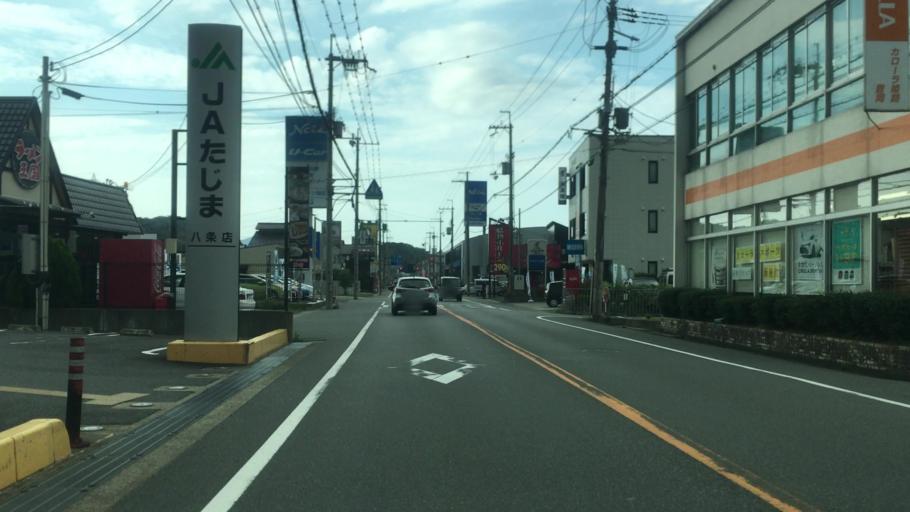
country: JP
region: Hyogo
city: Toyooka
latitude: 35.5256
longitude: 134.8212
